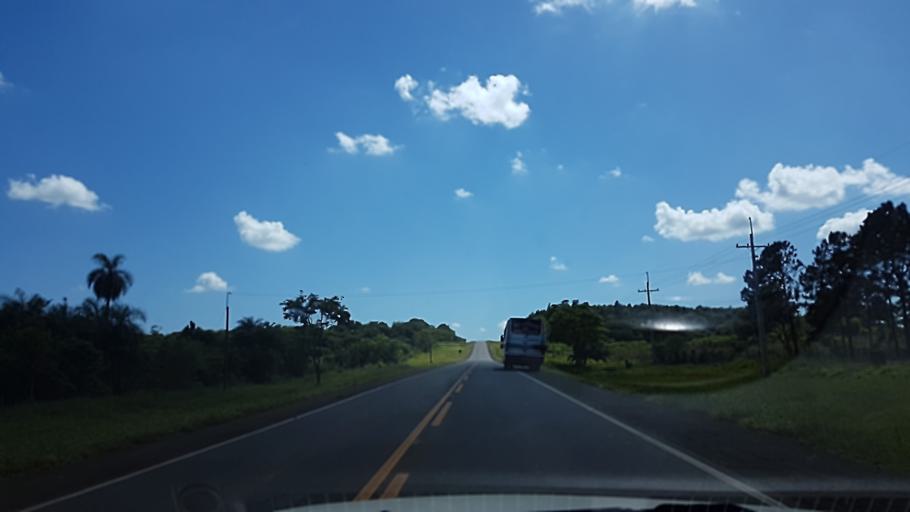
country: PY
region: Itapua
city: Carmen del Parana
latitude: -27.2193
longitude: -56.0988
